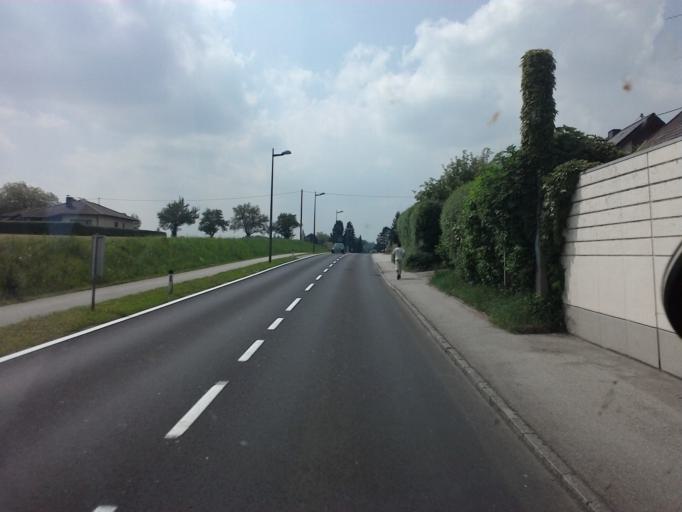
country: AT
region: Upper Austria
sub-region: Wels-Land
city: Sattledt
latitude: 48.0724
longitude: 14.0665
